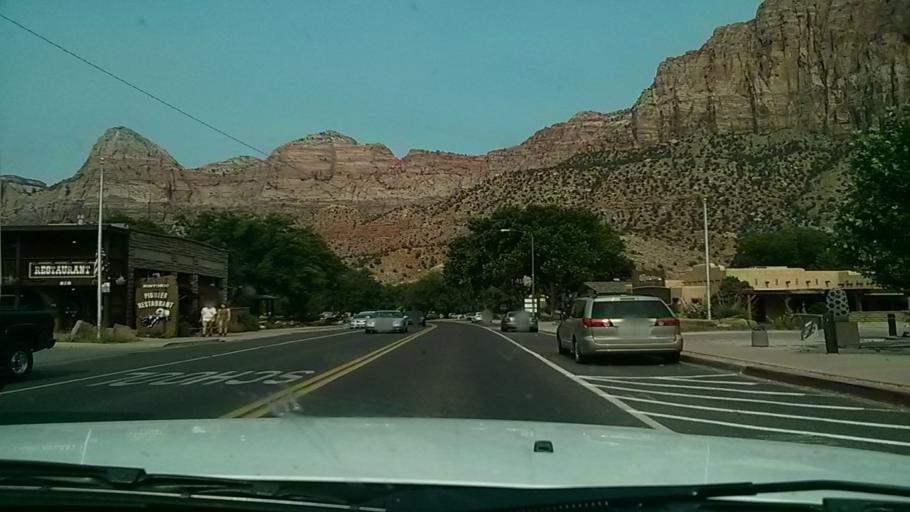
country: US
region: Utah
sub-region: Washington County
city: Hildale
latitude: 37.1889
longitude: -112.9985
